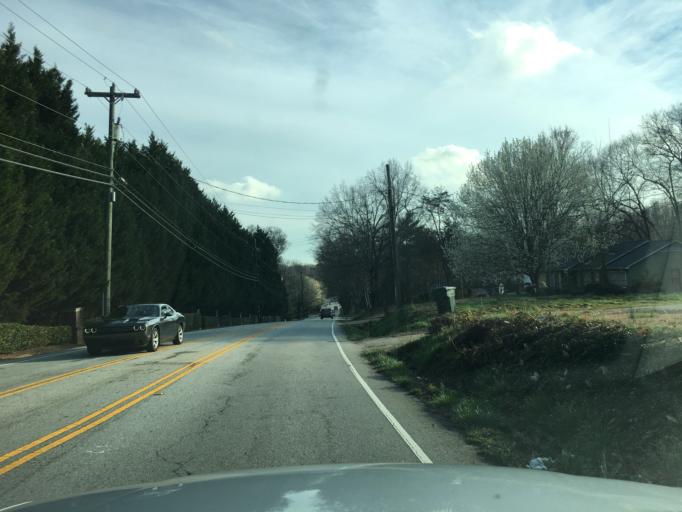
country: US
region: South Carolina
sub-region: Greenville County
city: Taylors
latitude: 34.8880
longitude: -82.2905
